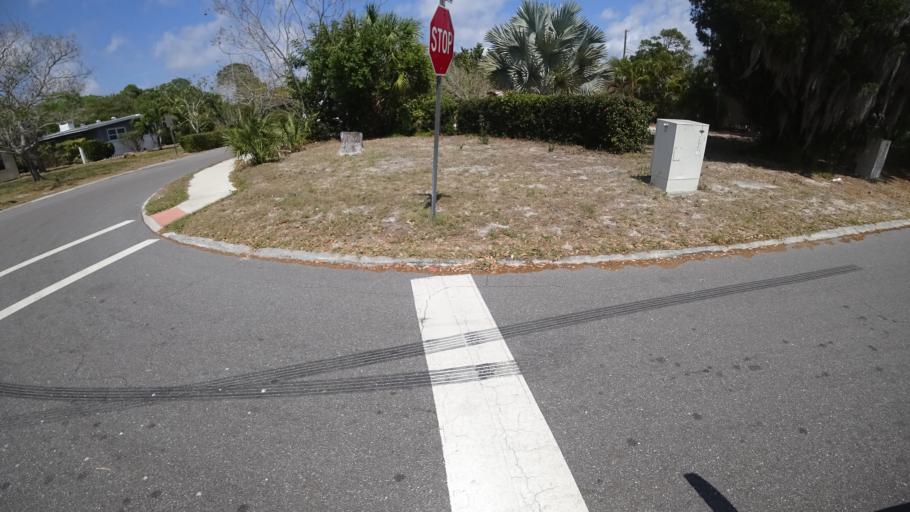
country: US
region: Florida
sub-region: Manatee County
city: Bayshore Gardens
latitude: 27.4306
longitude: -82.5814
